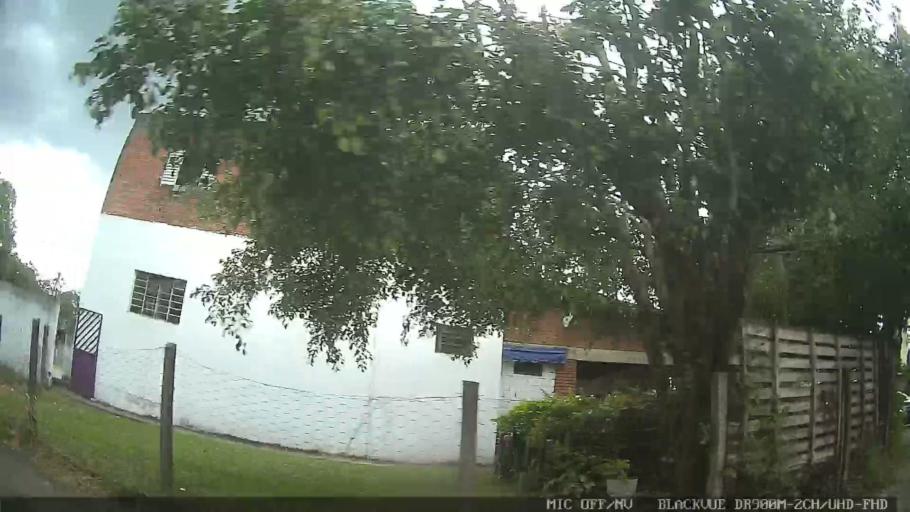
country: BR
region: Sao Paulo
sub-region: Suzano
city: Suzano
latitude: -23.5725
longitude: -46.2962
